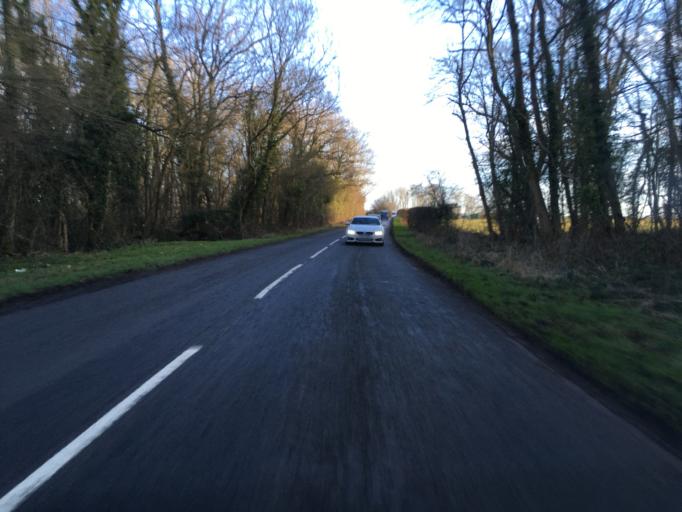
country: GB
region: England
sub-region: Warwickshire
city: Stratford-upon-Avon
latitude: 52.2425
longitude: -1.7228
